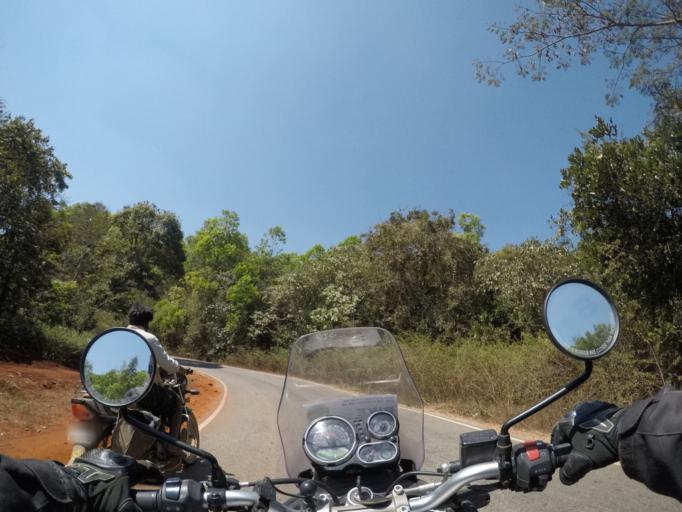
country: IN
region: Karnataka
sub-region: Hassan
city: Sakleshpur
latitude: 12.9637
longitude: 75.7360
